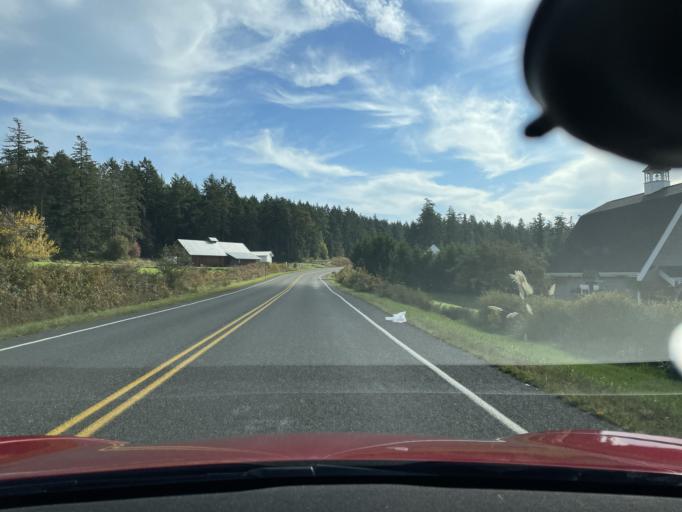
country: US
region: Washington
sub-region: San Juan County
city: Friday Harbor
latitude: 48.6088
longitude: -123.1386
